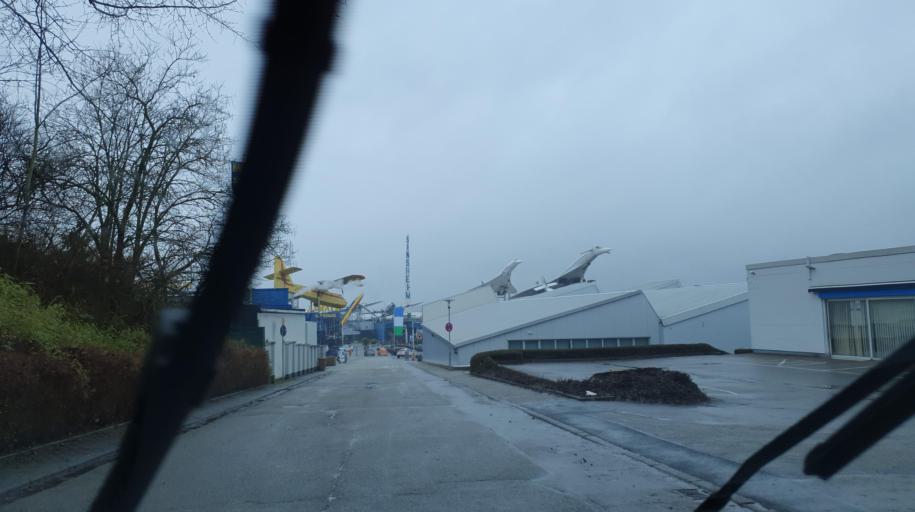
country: DE
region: Baden-Wuerttemberg
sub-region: Karlsruhe Region
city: Sinsheim
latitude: 49.2374
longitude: 8.8997
